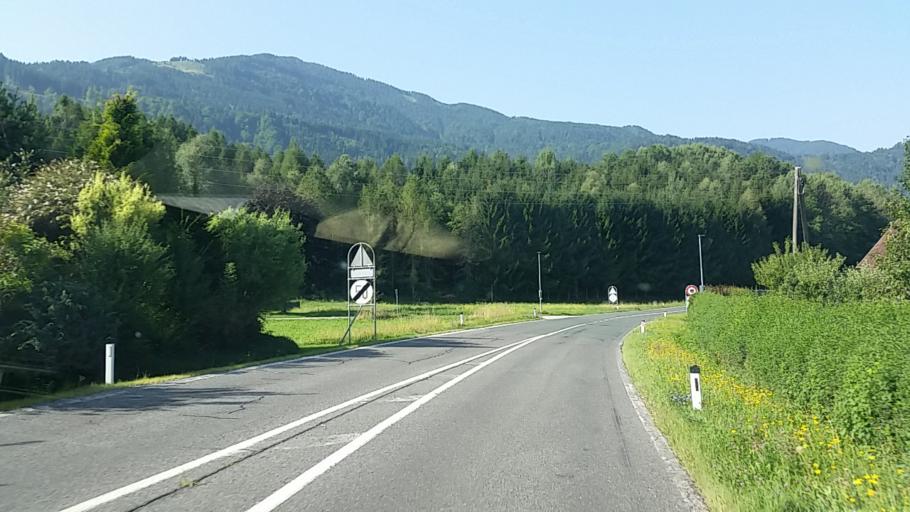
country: AT
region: Carinthia
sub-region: Politischer Bezirk Villach Land
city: Arnoldstein
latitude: 46.5482
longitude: 13.7857
